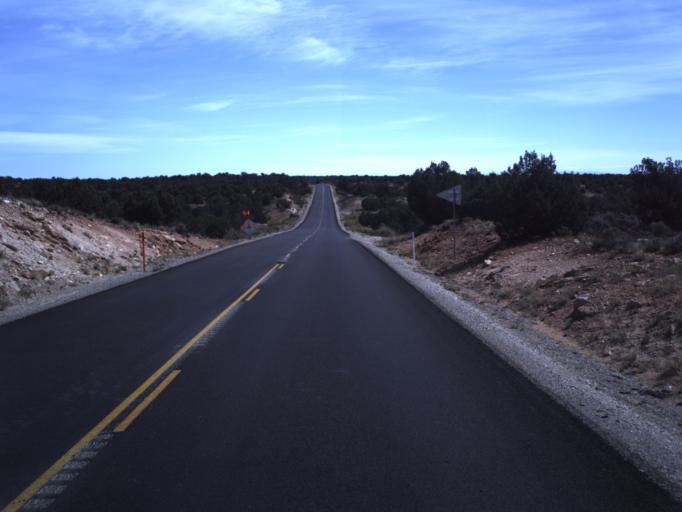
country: US
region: Utah
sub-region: San Juan County
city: Blanding
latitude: 37.5766
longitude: -109.5256
